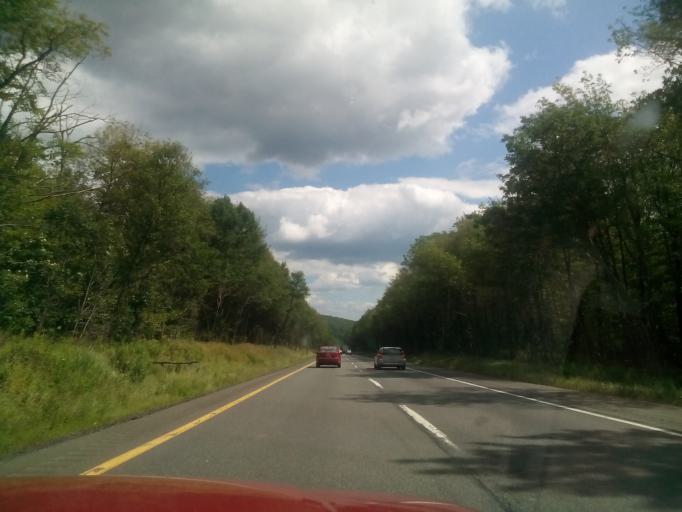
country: US
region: Pennsylvania
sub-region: Monroe County
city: Tannersville
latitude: 41.0591
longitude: -75.3274
